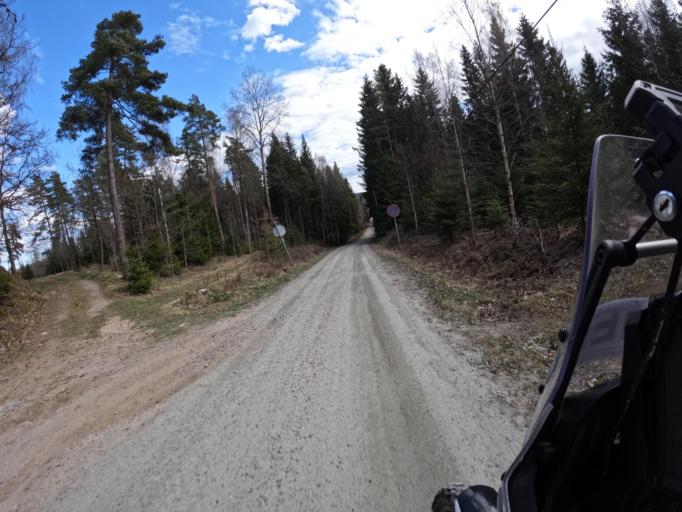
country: SE
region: Vaestra Goetaland
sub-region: Ulricehamns Kommun
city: Ulricehamn
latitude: 57.8276
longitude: 13.4080
